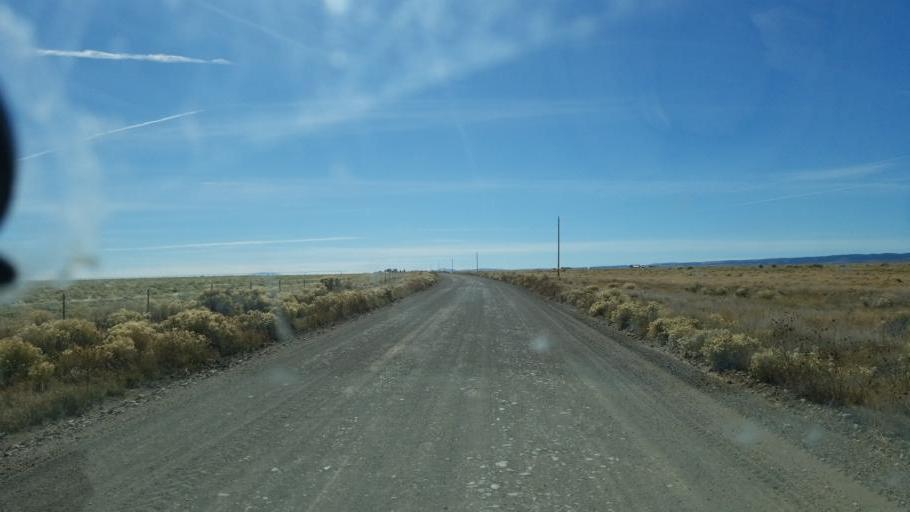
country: US
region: Colorado
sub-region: Rio Grande County
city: Monte Vista
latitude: 37.3977
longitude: -106.1493
